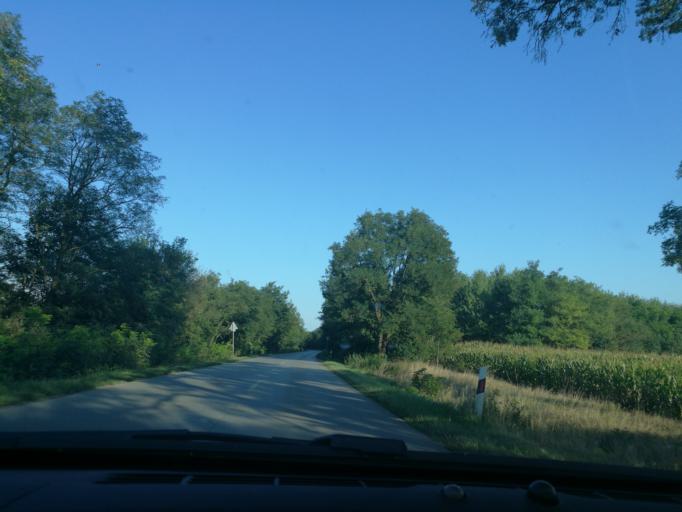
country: HU
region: Szabolcs-Szatmar-Bereg
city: Buj
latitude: 48.0613
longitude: 21.6514
